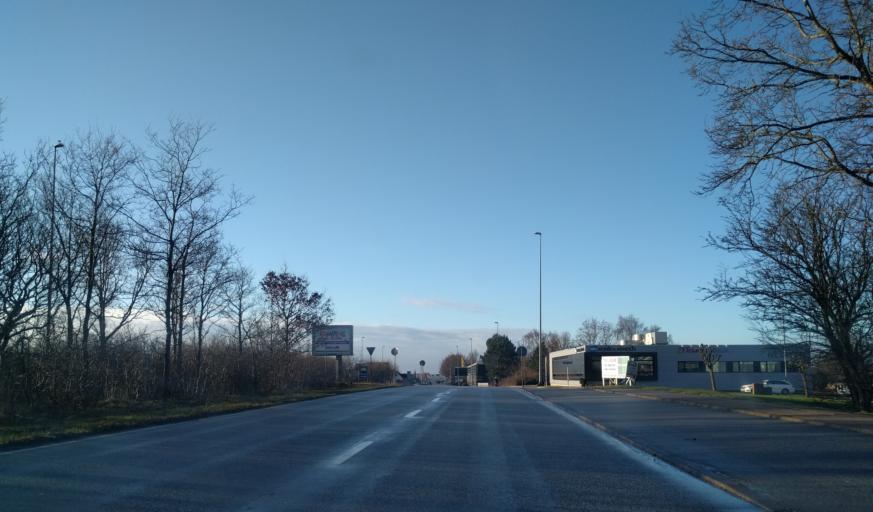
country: DK
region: North Denmark
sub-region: Alborg Kommune
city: Aalborg
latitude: 57.0194
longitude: 9.8990
